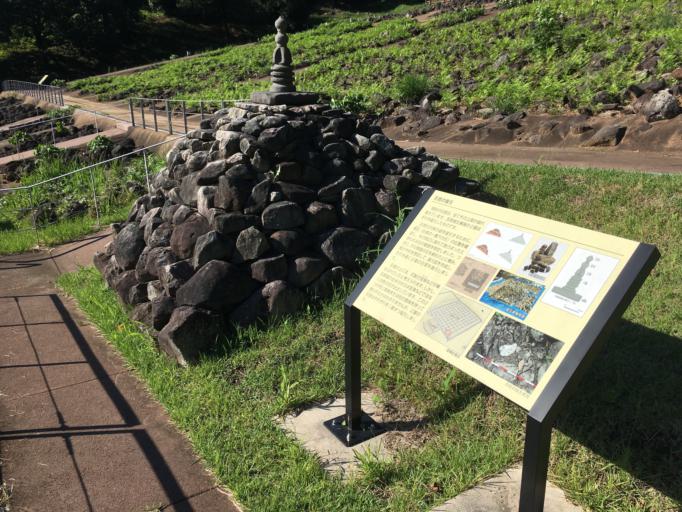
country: JP
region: Kumamoto
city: Kumamoto
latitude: 32.7992
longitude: 130.6544
